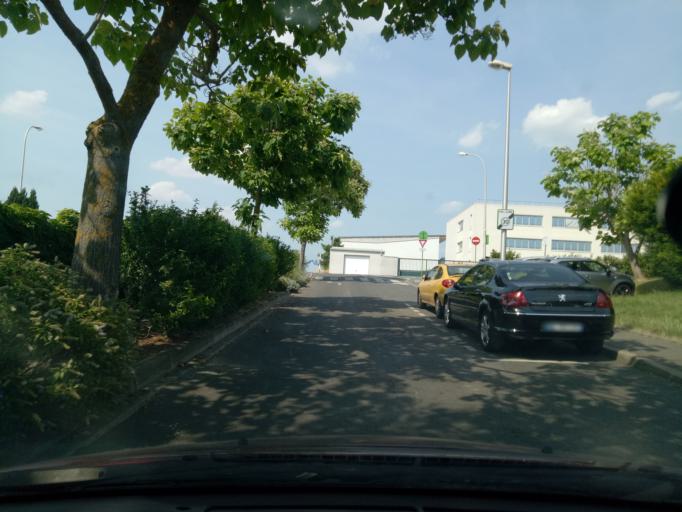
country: FR
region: Ile-de-France
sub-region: Departement des Yvelines
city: Montesson
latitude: 48.9124
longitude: 2.1487
